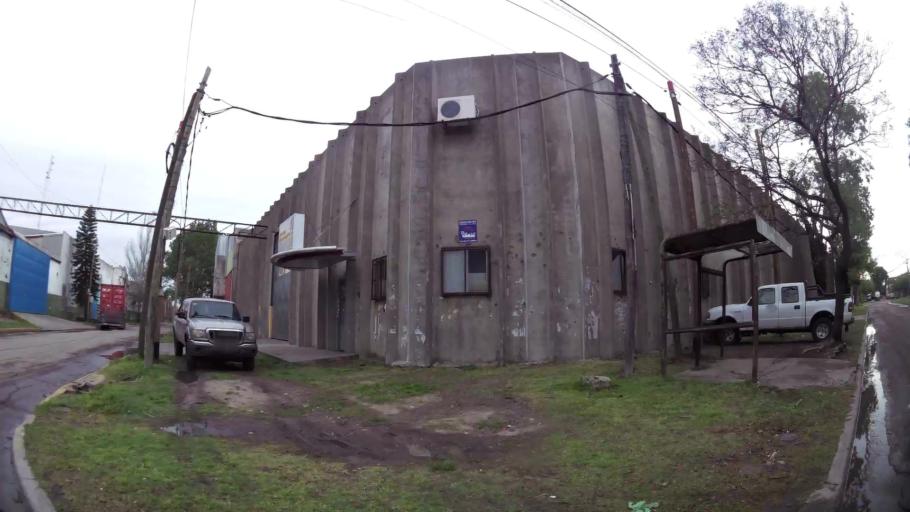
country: AR
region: Buenos Aires
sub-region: Partido de Lanus
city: Lanus
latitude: -34.7093
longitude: -58.3615
